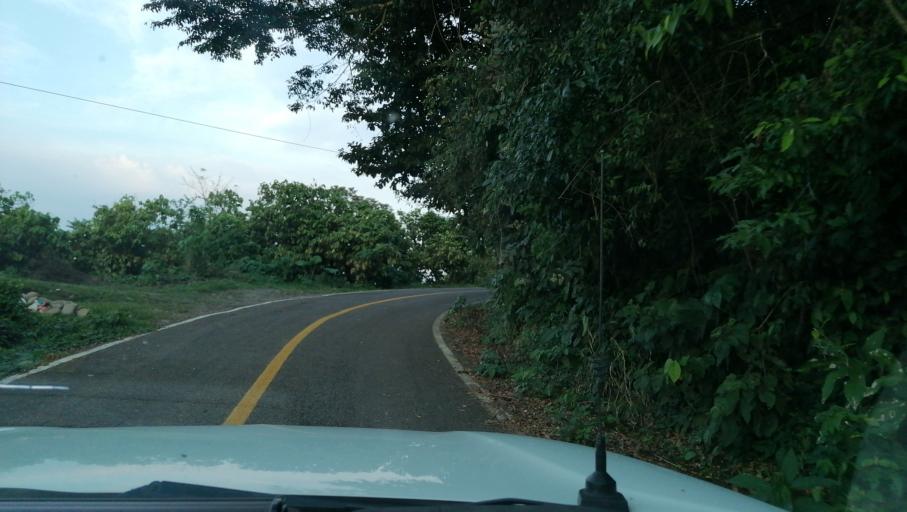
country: MX
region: Chiapas
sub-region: Juarez
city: El Triunfo 1ra. Seccion (Cardona)
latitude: 17.5073
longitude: -93.2304
